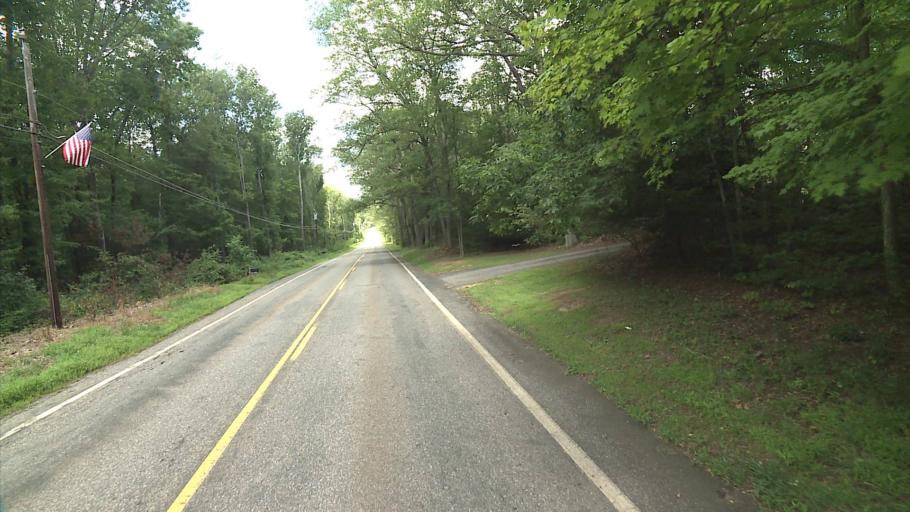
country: US
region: Connecticut
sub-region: Tolland County
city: Stafford
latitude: 41.9283
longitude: -72.1933
